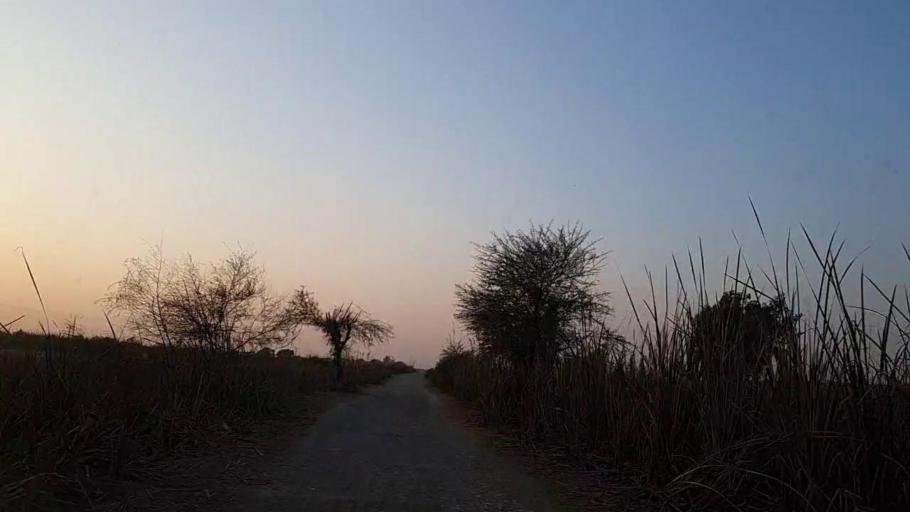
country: PK
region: Sindh
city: Bhit Shah
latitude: 25.9202
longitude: 68.4948
